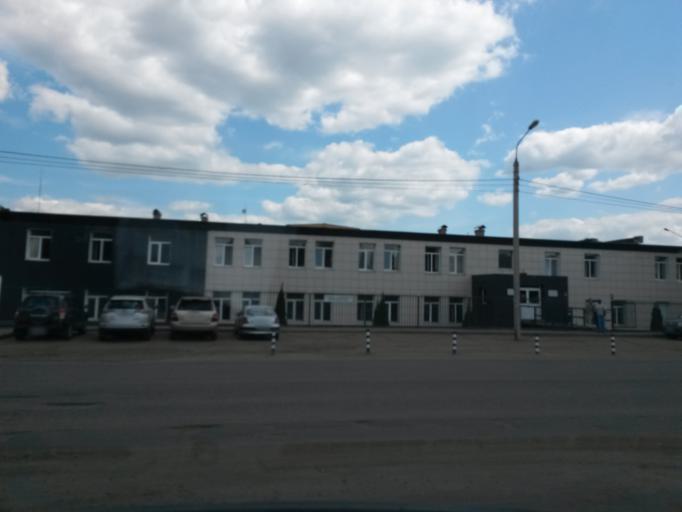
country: RU
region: Jaroslavl
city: Yaroslavl
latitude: 57.5773
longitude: 39.8866
